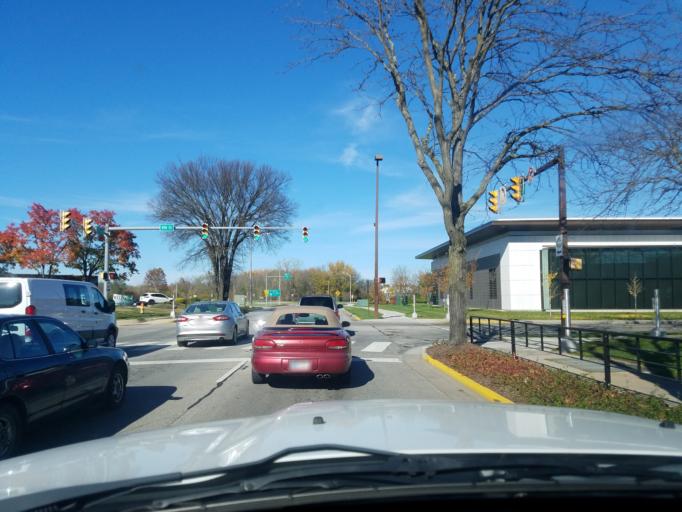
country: US
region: Indiana
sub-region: Bartholomew County
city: Columbus
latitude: 39.2064
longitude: -85.9240
